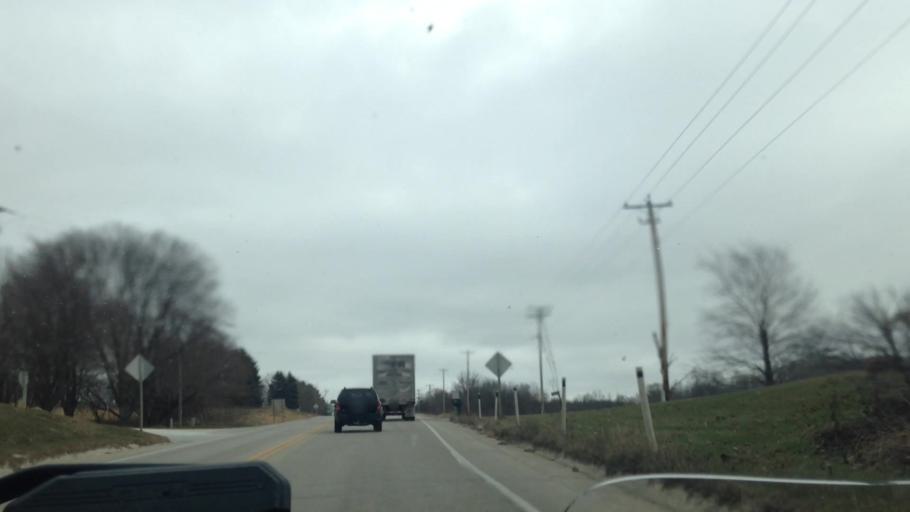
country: US
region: Wisconsin
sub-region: Dodge County
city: Mayville
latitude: 43.4428
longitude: -88.5406
